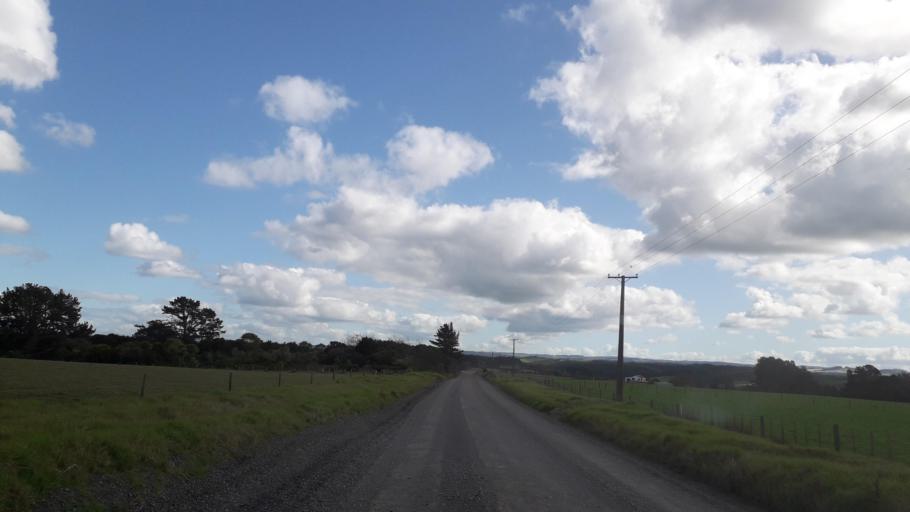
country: NZ
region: Northland
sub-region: Far North District
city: Kerikeri
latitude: -35.1307
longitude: 174.0039
